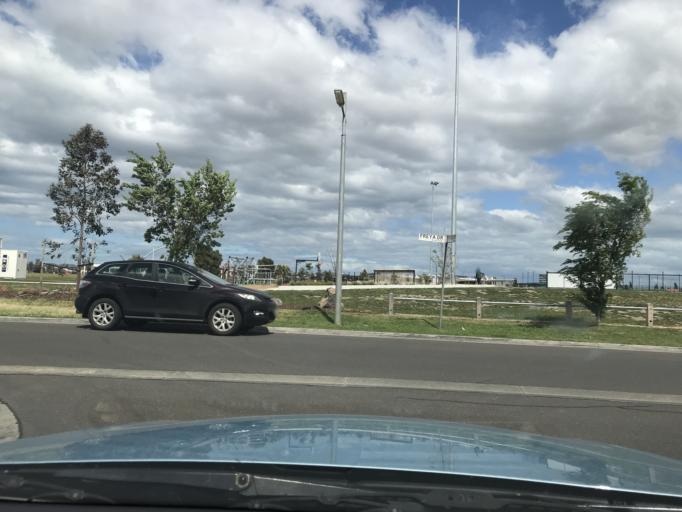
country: AU
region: Victoria
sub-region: Wyndham
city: Williams Landing
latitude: -37.8594
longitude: 144.7502
